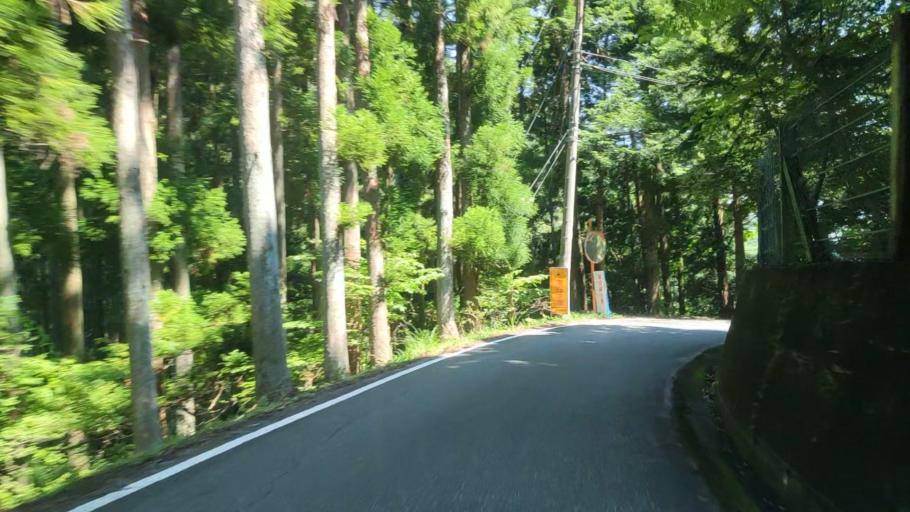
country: JP
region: Gifu
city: Godo
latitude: 35.6885
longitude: 136.5691
